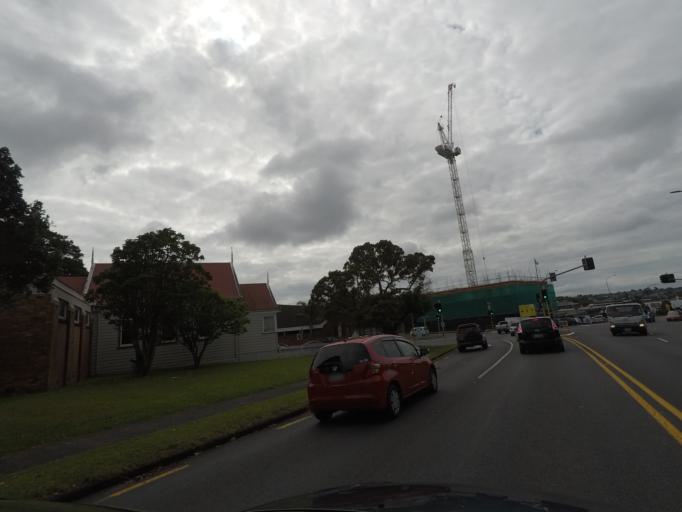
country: NZ
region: Auckland
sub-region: Auckland
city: Rosebank
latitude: -36.8748
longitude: 174.6270
